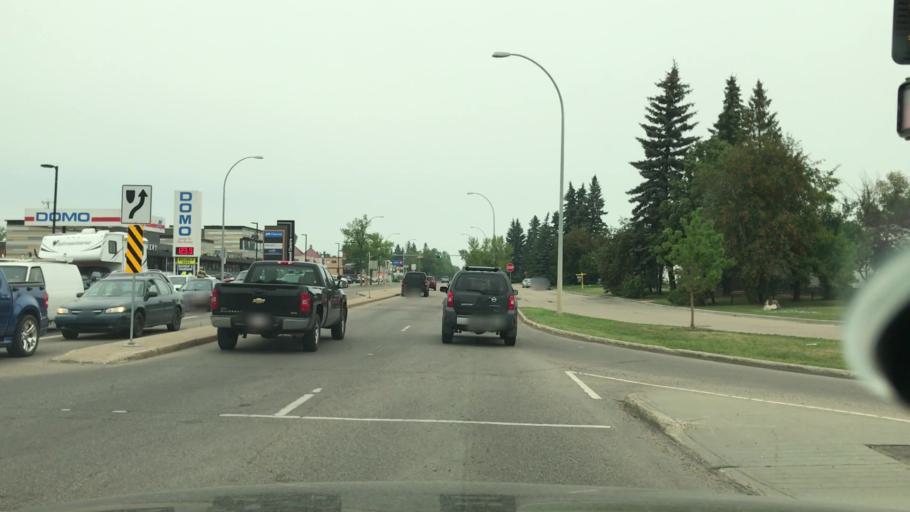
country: CA
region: Alberta
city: Edmonton
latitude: 53.5194
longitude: -113.5778
